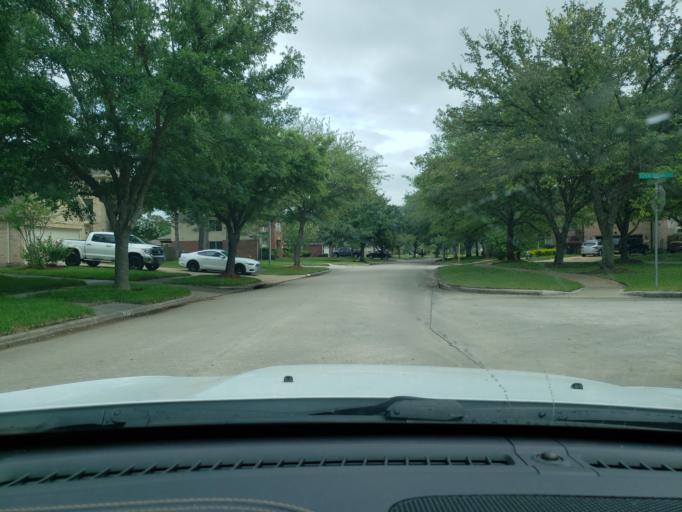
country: US
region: Texas
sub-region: Harris County
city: Jersey Village
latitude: 29.9226
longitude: -95.5675
